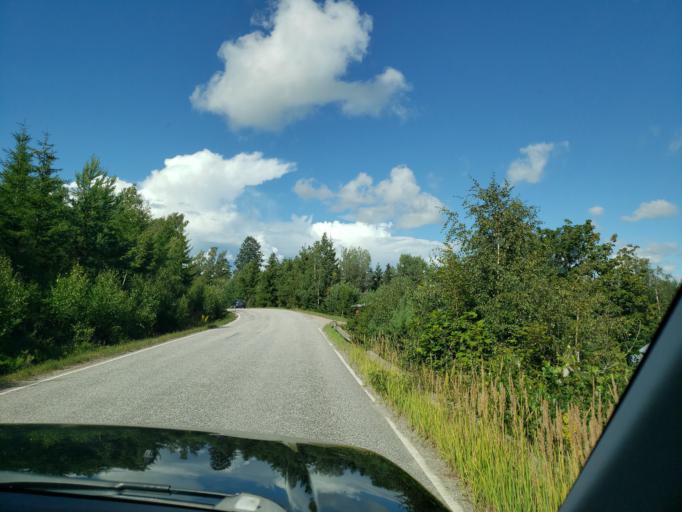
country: FI
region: Varsinais-Suomi
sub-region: Aboland-Turunmaa
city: Dragsfjaerd
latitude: 60.0633
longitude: 22.4516
